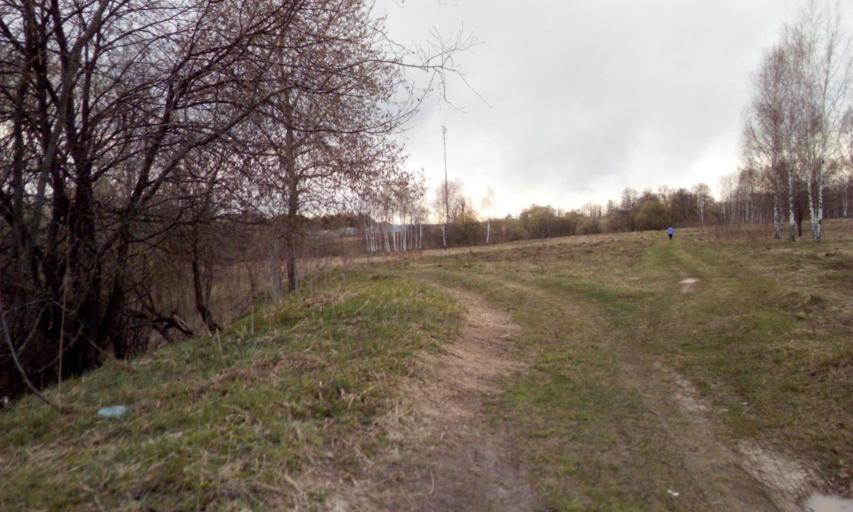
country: RU
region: Moskovskaya
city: Troitsk
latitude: 55.5150
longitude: 37.2674
